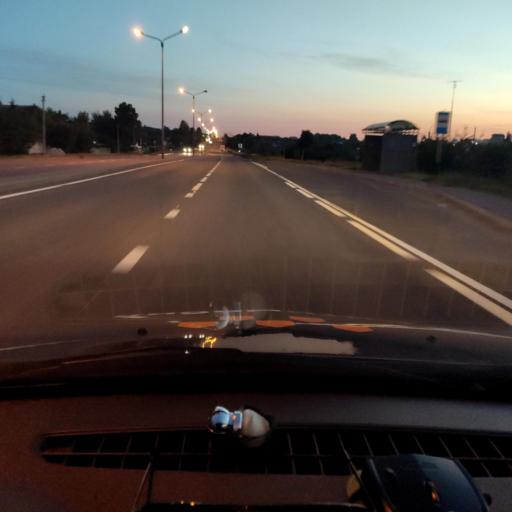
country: RU
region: Belgorod
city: Gubkin
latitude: 51.2674
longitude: 37.5623
